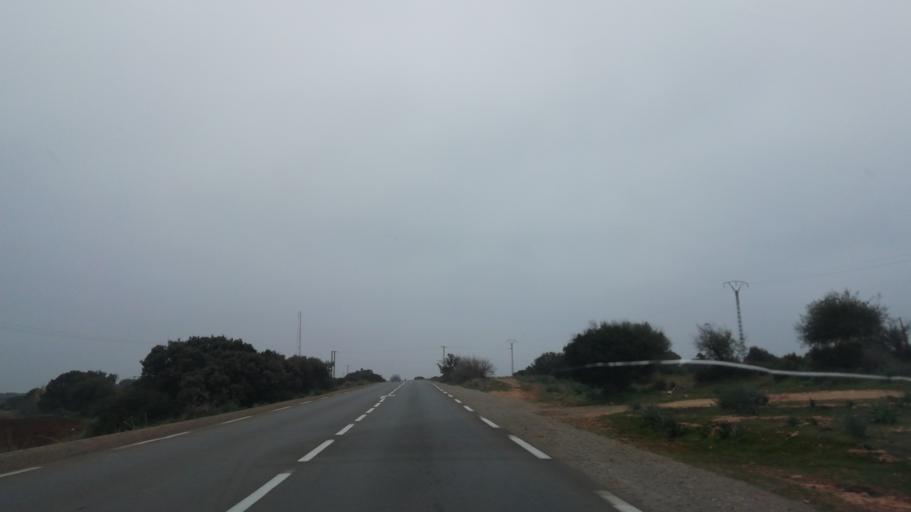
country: DZ
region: Mascara
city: Oued el Abtal
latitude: 35.3049
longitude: 0.4285
